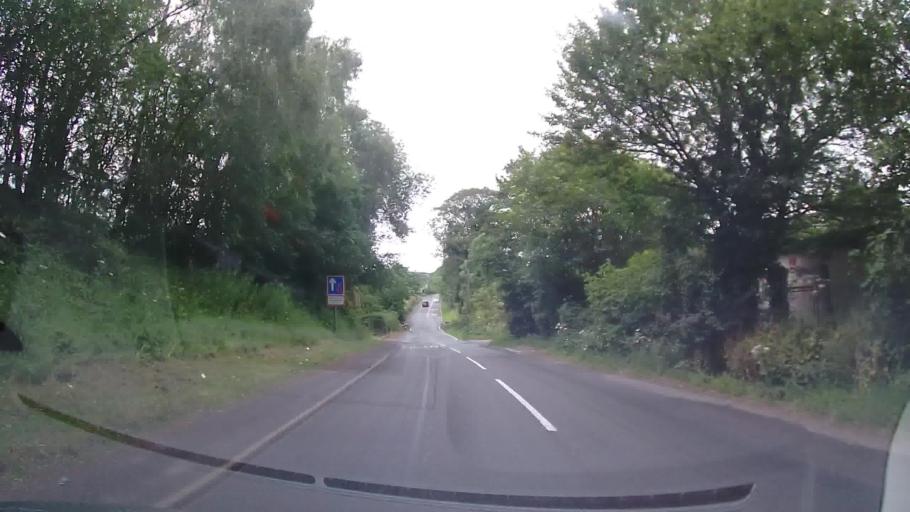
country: GB
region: England
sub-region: Shropshire
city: Gobowen
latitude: 52.9184
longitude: -3.0284
